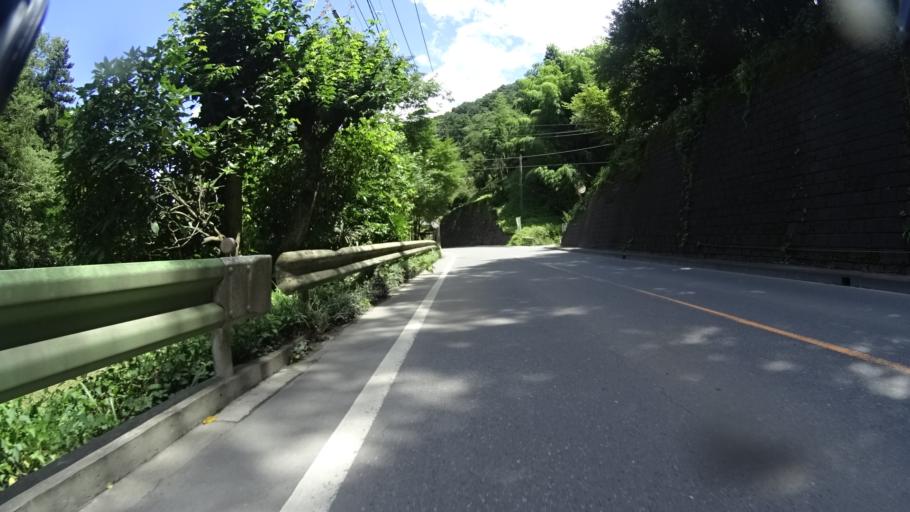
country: JP
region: Tokyo
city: Ome
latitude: 35.8191
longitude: 139.2361
